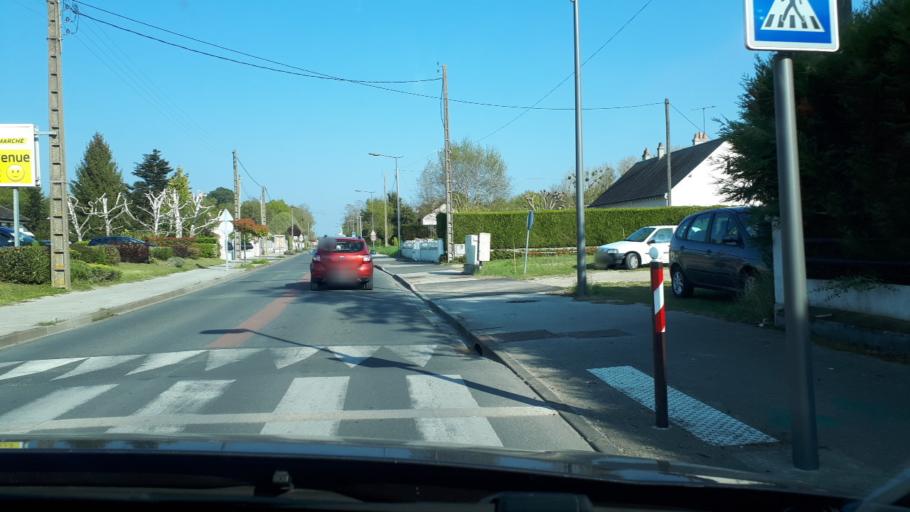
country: FR
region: Centre
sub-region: Departement d'Indre-et-Loire
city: Blere
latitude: 47.3247
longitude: 1.0079
